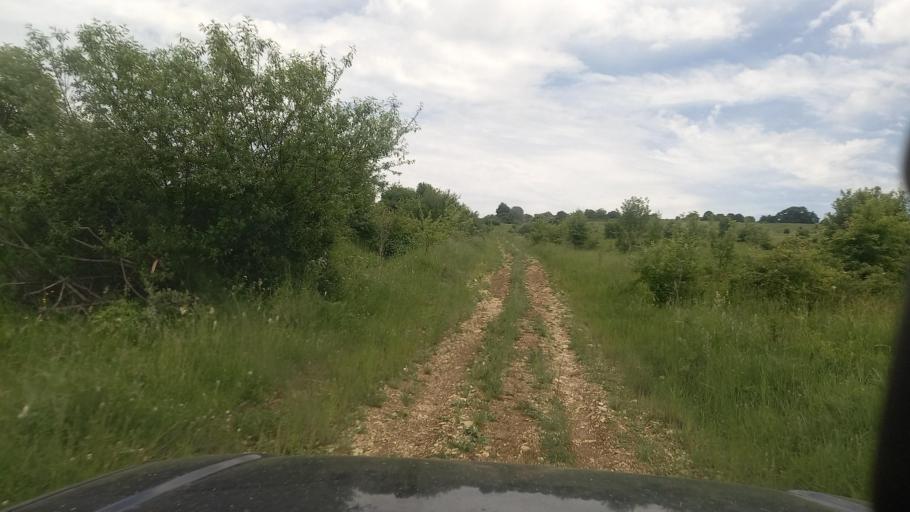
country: RU
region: Karachayevo-Cherkesiya
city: Pregradnaya
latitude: 44.0856
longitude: 41.2103
